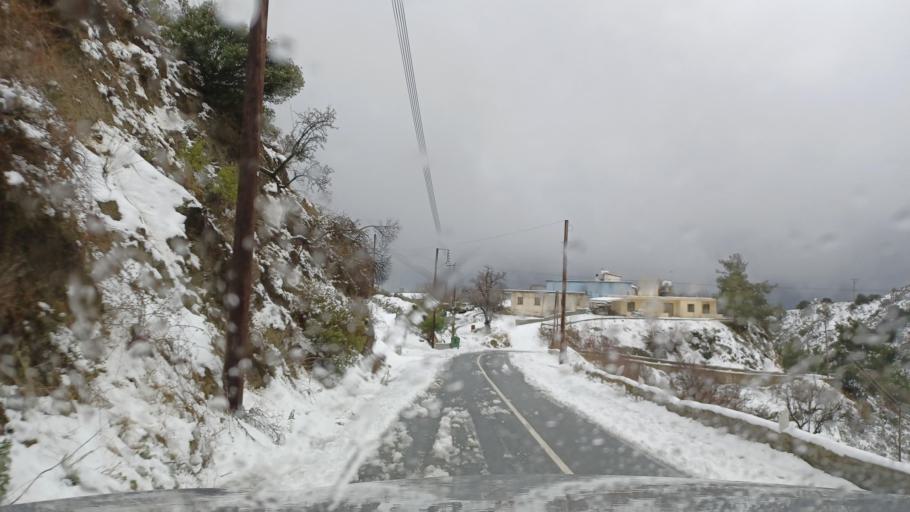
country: CY
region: Limassol
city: Pelendri
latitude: 34.9034
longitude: 32.9643
